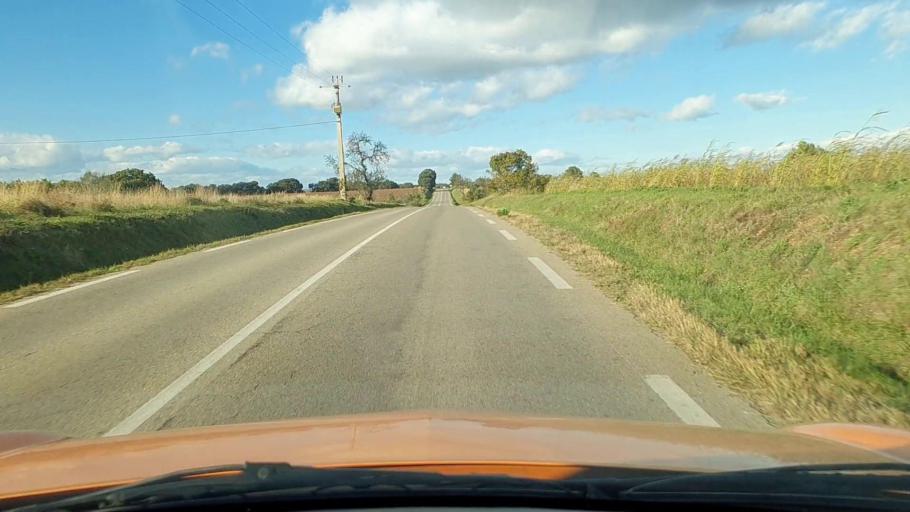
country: FR
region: Languedoc-Roussillon
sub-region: Departement du Gard
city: Vauvert
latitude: 43.6714
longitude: 4.2819
